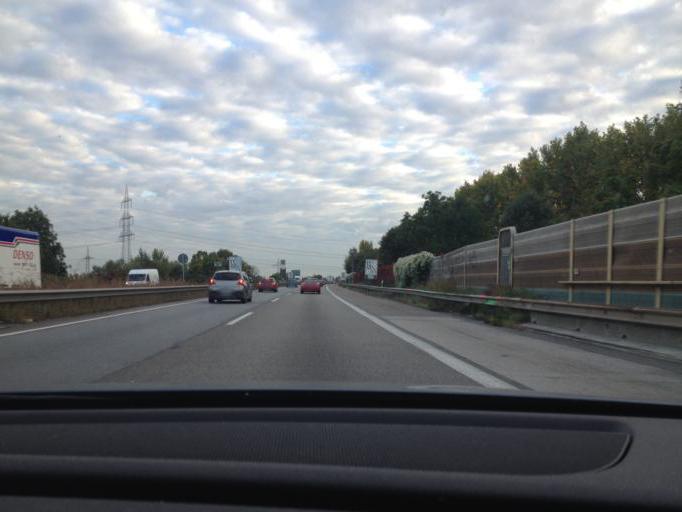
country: DE
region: Rheinland-Pfalz
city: Hessheim
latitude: 49.5435
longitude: 8.3160
